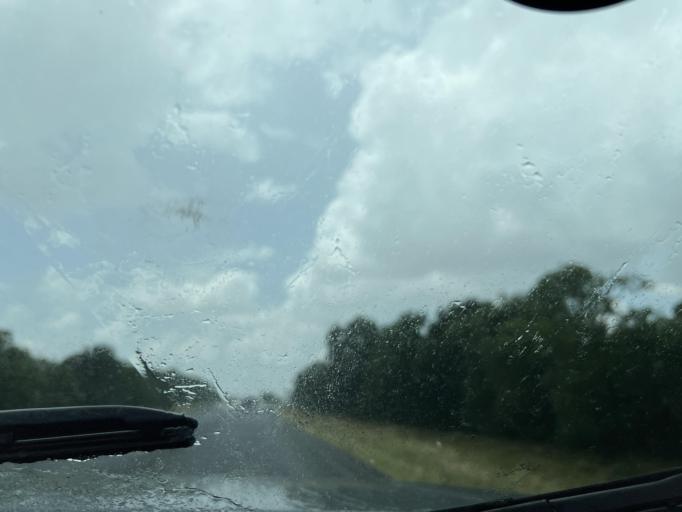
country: US
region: Texas
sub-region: Wise County
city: Boyd
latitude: 33.1317
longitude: -97.6464
